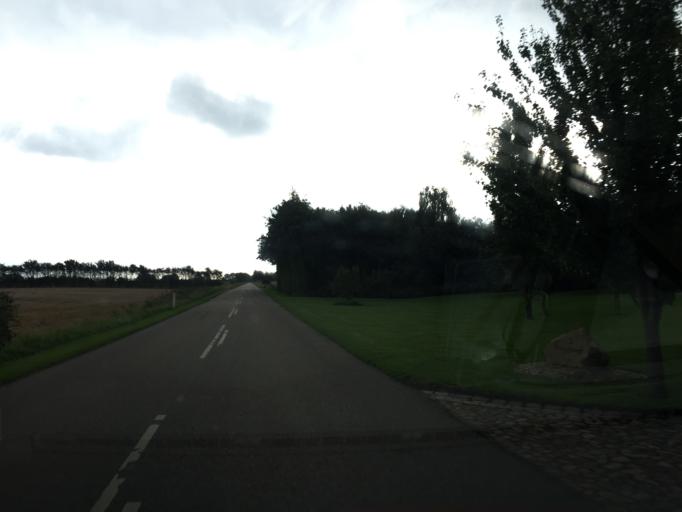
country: DK
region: South Denmark
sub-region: Sonderborg Kommune
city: Dybbol
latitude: 54.9808
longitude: 9.6990
